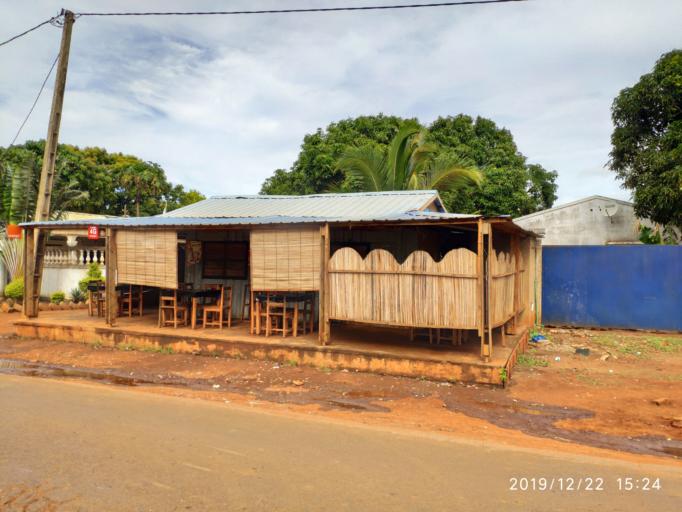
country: MG
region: Diana
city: Antsiranana
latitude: -12.3522
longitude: 49.2982
